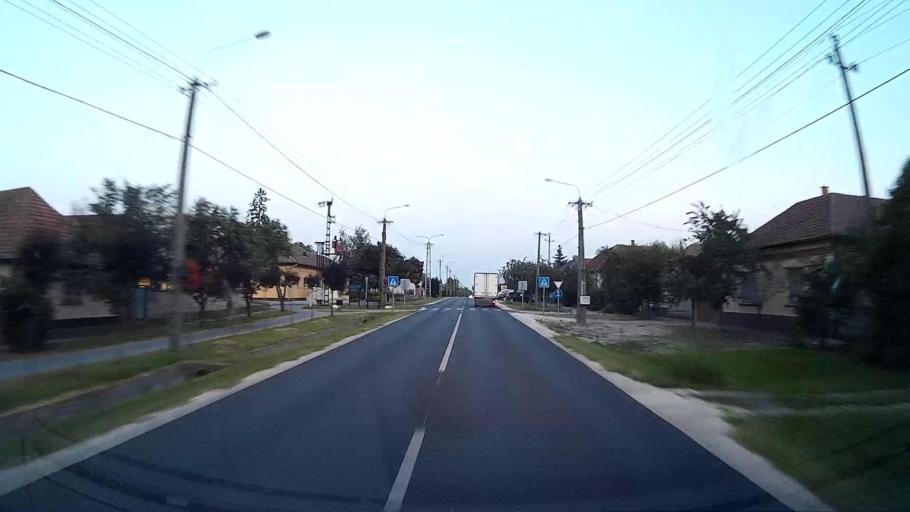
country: HU
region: Pest
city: Cegledbercel
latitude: 47.2161
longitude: 19.6748
